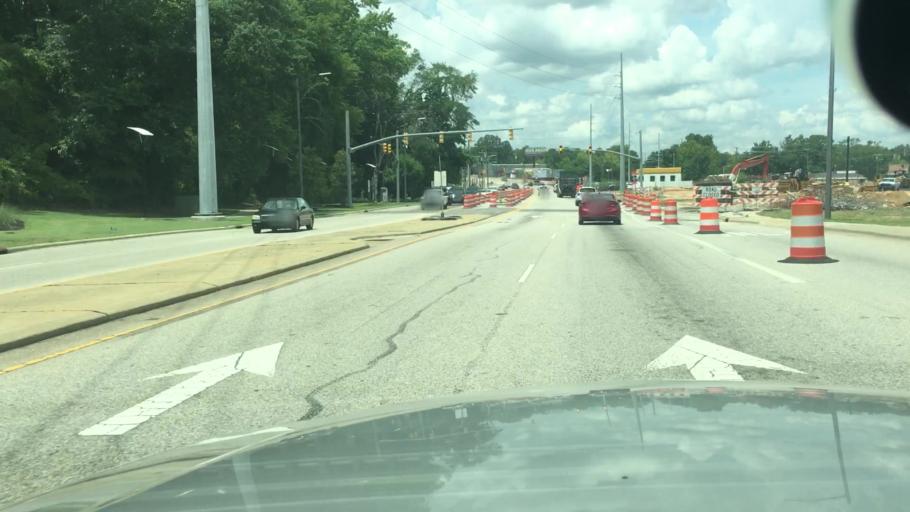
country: US
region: North Carolina
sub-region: Cumberland County
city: Fayetteville
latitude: 35.0587
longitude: -78.8865
